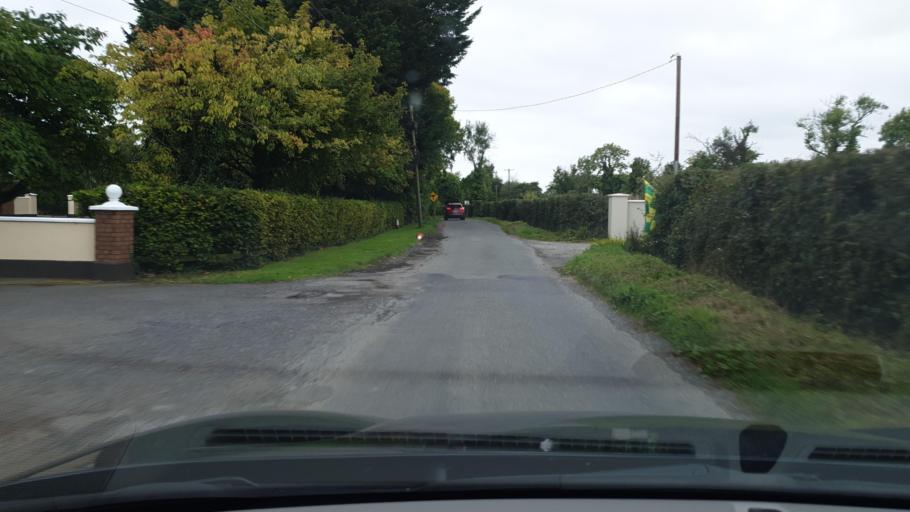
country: IE
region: Leinster
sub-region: An Mhi
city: Dunshaughlin
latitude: 53.5233
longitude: -6.5117
